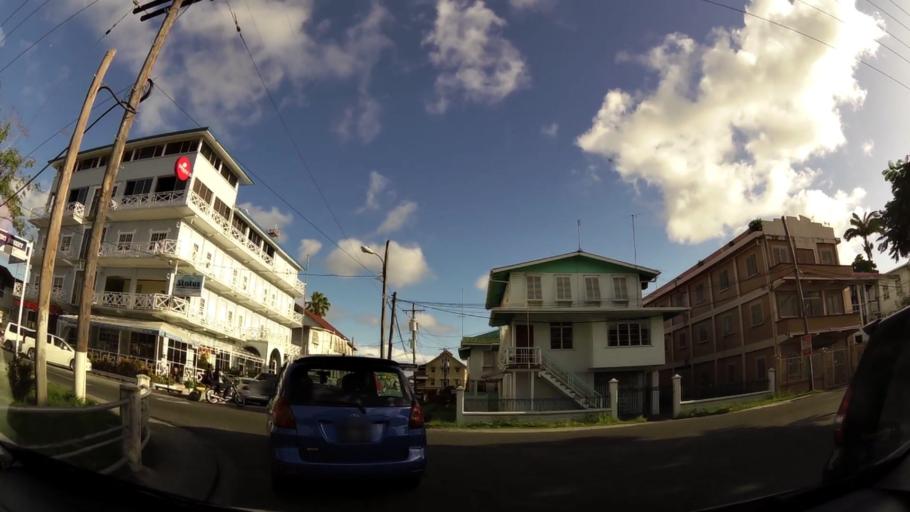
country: GY
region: Demerara-Mahaica
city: Georgetown
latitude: 6.8067
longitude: -58.1542
